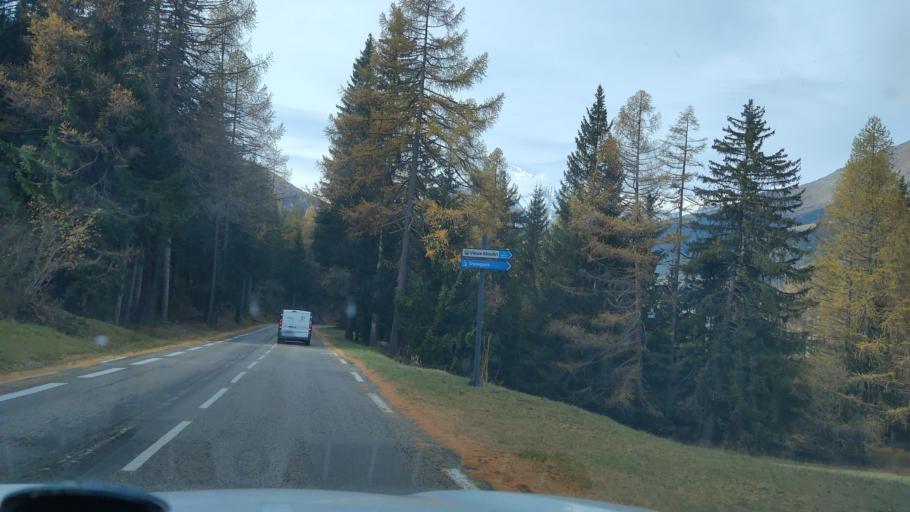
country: IT
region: Piedmont
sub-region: Provincia di Torino
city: Moncenisio
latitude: 45.2810
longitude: 6.9089
